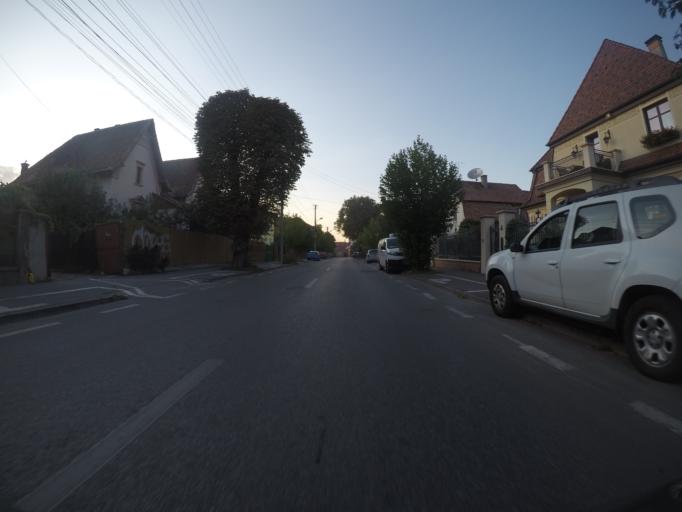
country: RO
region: Sibiu
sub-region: Municipiul Sibiu
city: Sibiu
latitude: 45.7912
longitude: 24.1573
